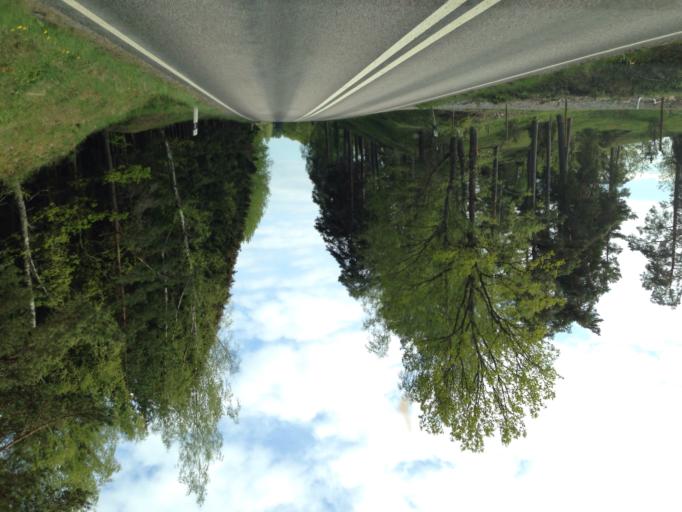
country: SE
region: Soedermanland
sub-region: Flens Kommun
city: Malmkoping
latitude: 58.9983
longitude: 16.8449
